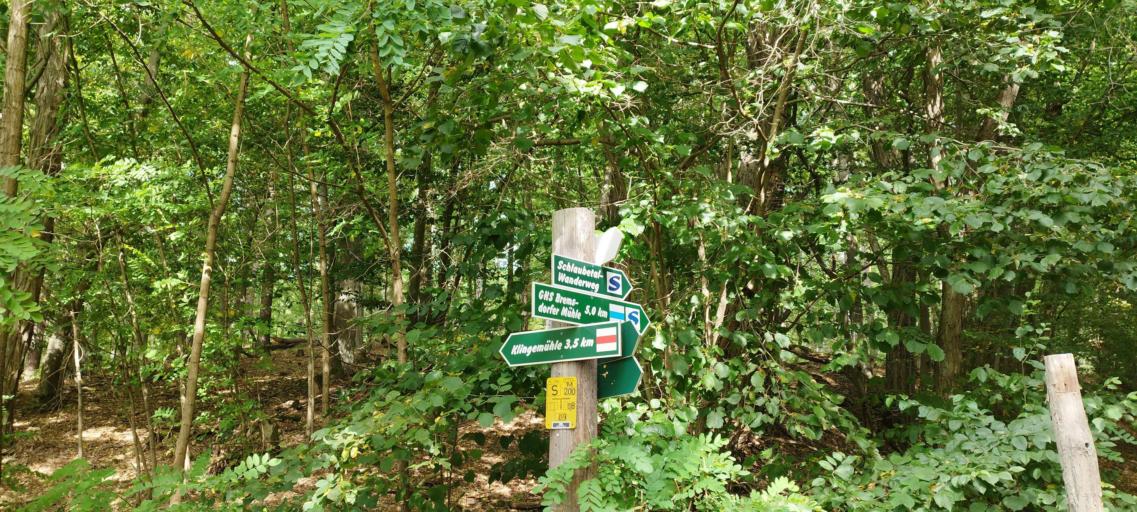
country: DE
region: Brandenburg
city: Mixdorf
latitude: 52.1071
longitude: 14.4760
